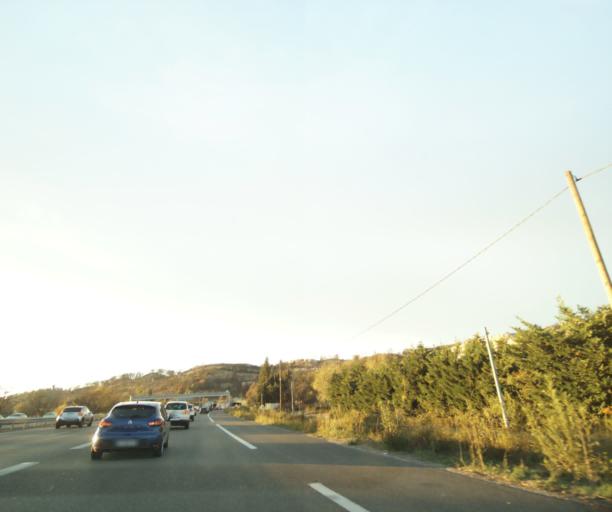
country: FR
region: Provence-Alpes-Cote d'Azur
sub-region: Departement des Bouches-du-Rhone
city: Les Pennes-Mirabeau
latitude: 43.4092
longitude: 5.2895
